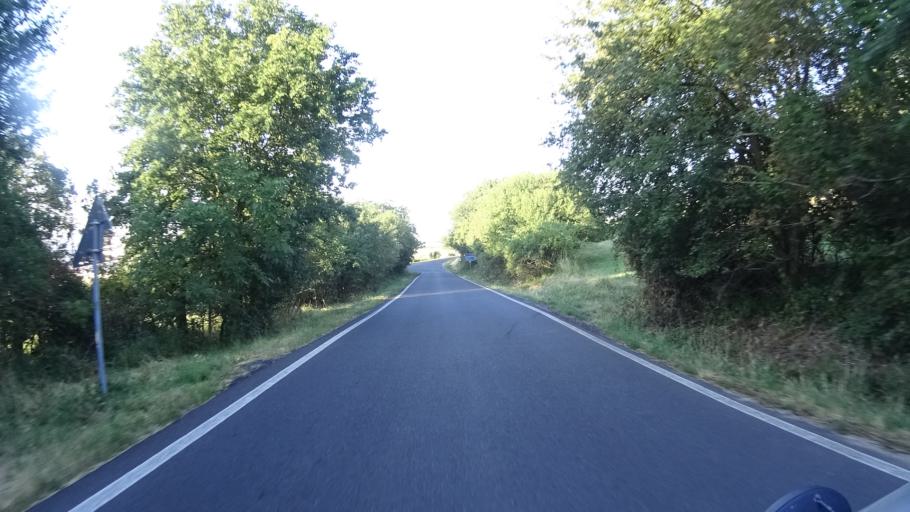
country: CZ
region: Ustecky
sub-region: Okres Litomerice
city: Litomerice
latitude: 50.5639
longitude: 14.1209
